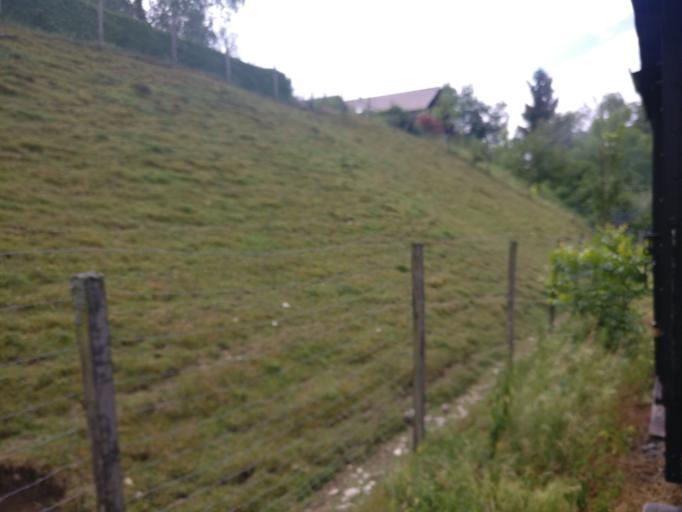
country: AT
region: Upper Austria
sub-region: Politischer Bezirk Kirchdorf an der Krems
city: Gruenburg
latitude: 47.9879
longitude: 14.2797
